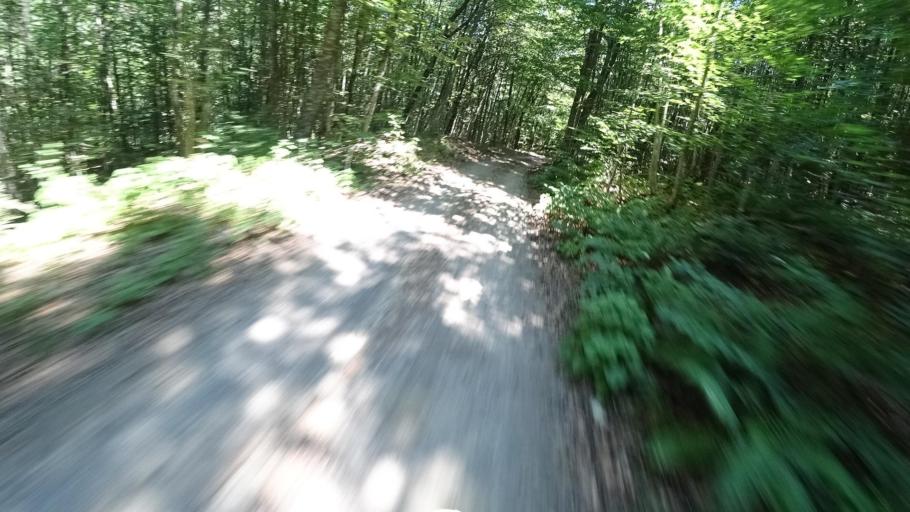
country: HR
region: Karlovacka
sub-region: Grad Ogulin
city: Ogulin
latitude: 45.3167
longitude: 15.2307
